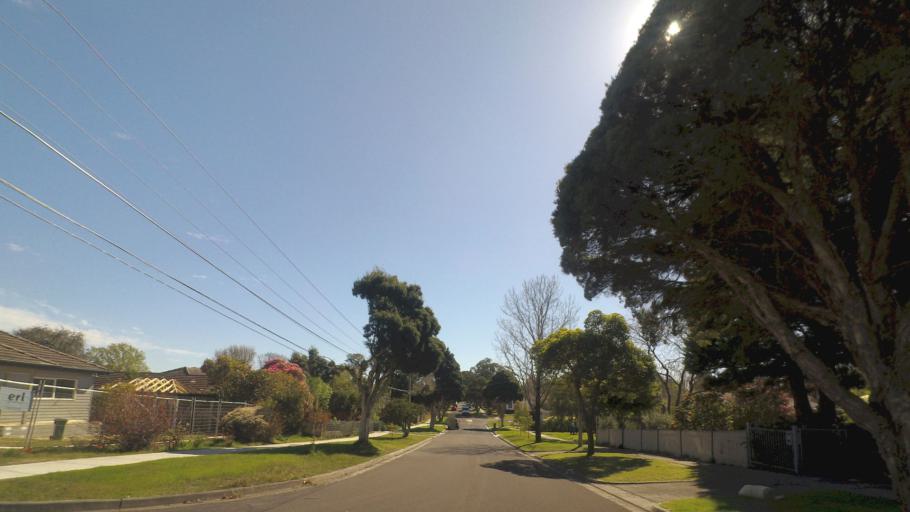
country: AU
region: Victoria
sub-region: Maroondah
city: Ringwood East
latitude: -37.8166
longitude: 145.2454
